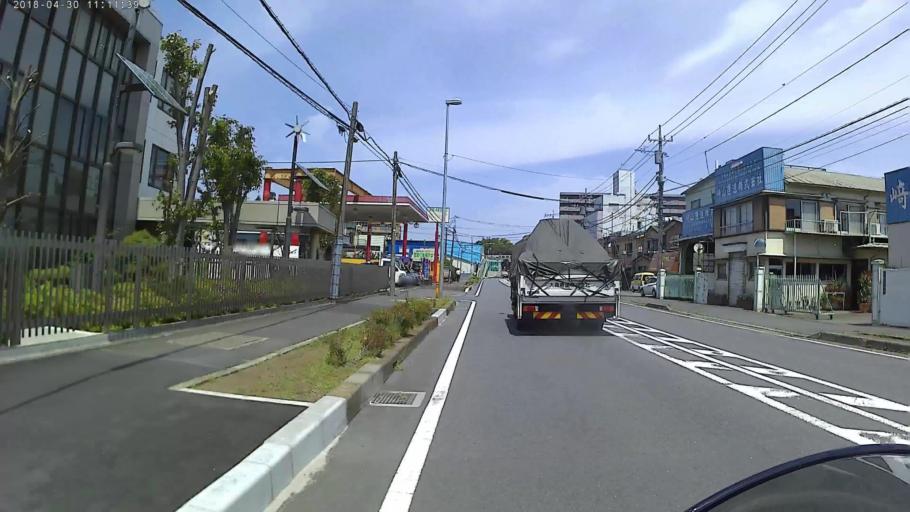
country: JP
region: Kanagawa
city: Minami-rinkan
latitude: 35.4658
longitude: 139.4301
